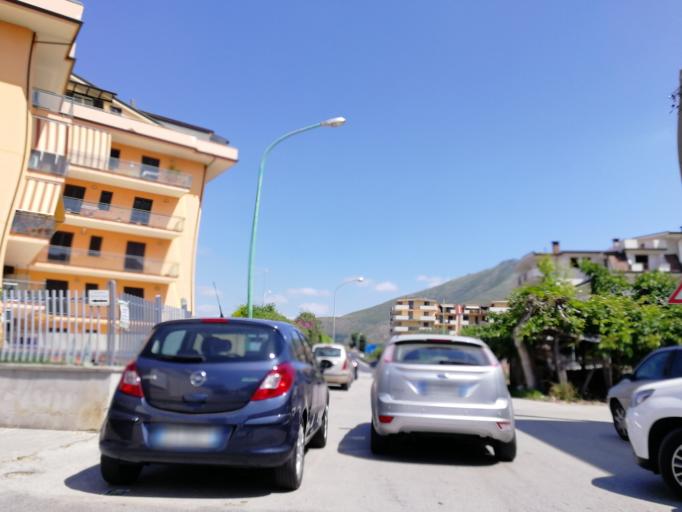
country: IT
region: Campania
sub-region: Provincia di Caserta
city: San Prisco
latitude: 41.0889
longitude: 14.2720
